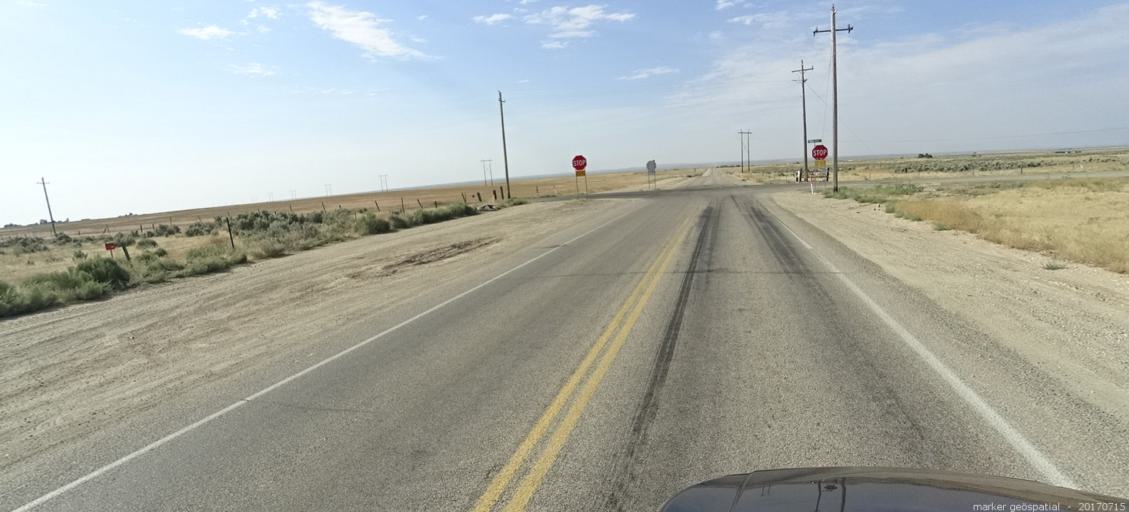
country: US
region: Idaho
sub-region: Ada County
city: Boise
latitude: 43.4594
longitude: -116.2344
